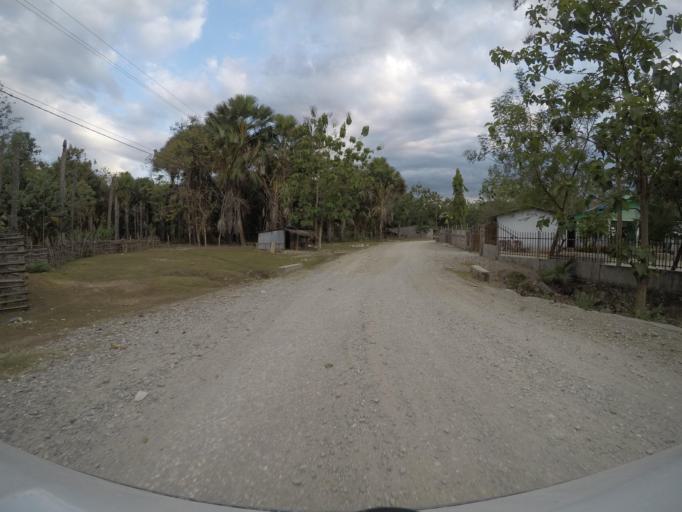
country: TL
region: Bobonaro
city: Maliana
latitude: -8.8777
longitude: 125.2123
